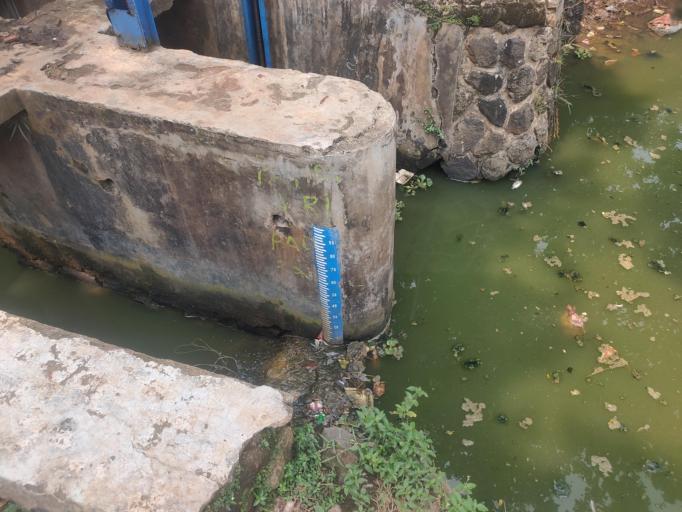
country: ID
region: West Java
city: Parung
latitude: -6.4235
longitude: 106.7006
